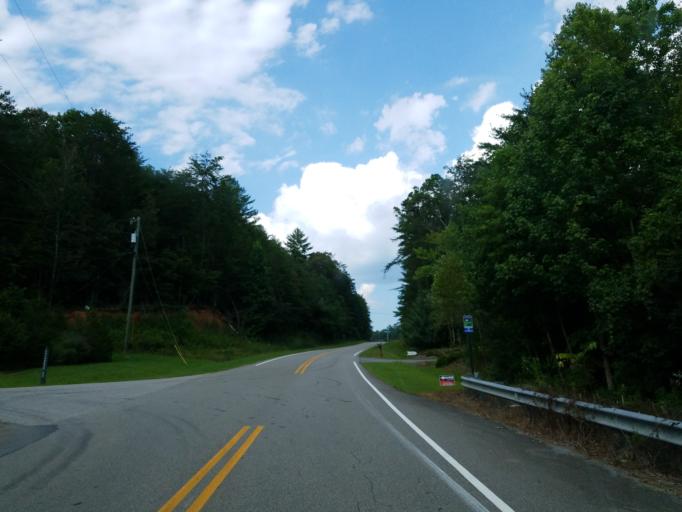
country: US
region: Georgia
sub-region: Gilmer County
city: Ellijay
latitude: 34.7593
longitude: -84.4255
